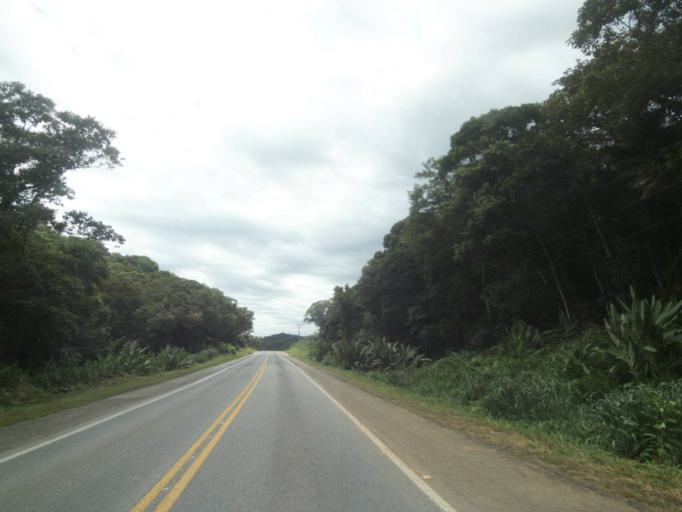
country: BR
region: Parana
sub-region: Antonina
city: Antonina
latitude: -25.4455
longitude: -48.7825
